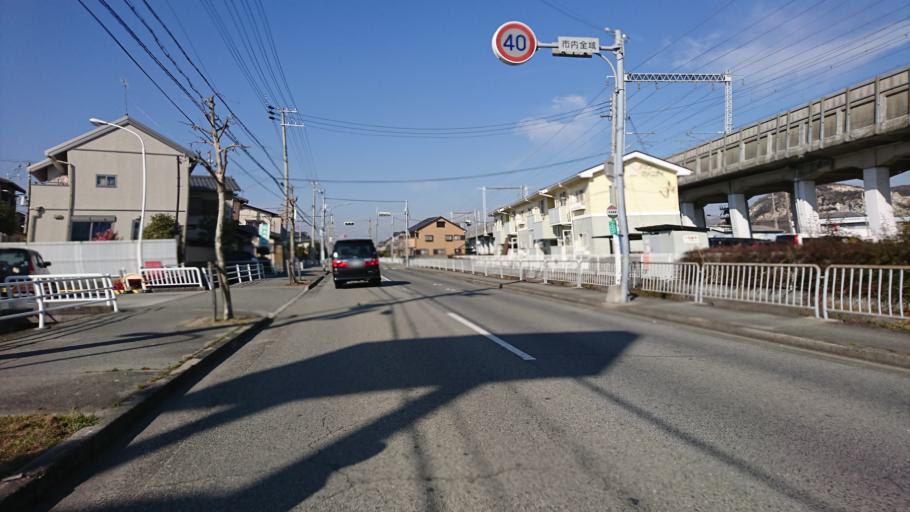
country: JP
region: Hyogo
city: Kakogawacho-honmachi
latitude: 34.7724
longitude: 134.7918
